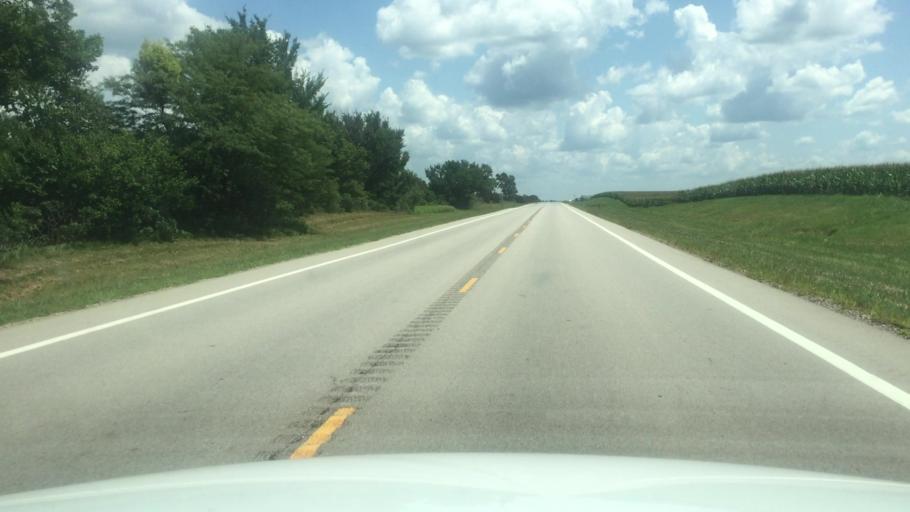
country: US
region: Kansas
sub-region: Brown County
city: Horton
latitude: 39.6581
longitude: -95.3767
